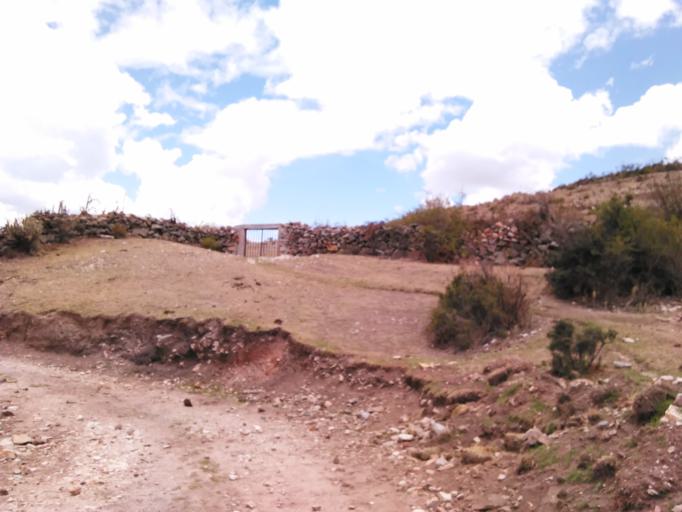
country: PE
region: Ayacucho
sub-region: Provincia de Victor Fajardo
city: Canaria
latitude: -13.8826
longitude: -73.9413
